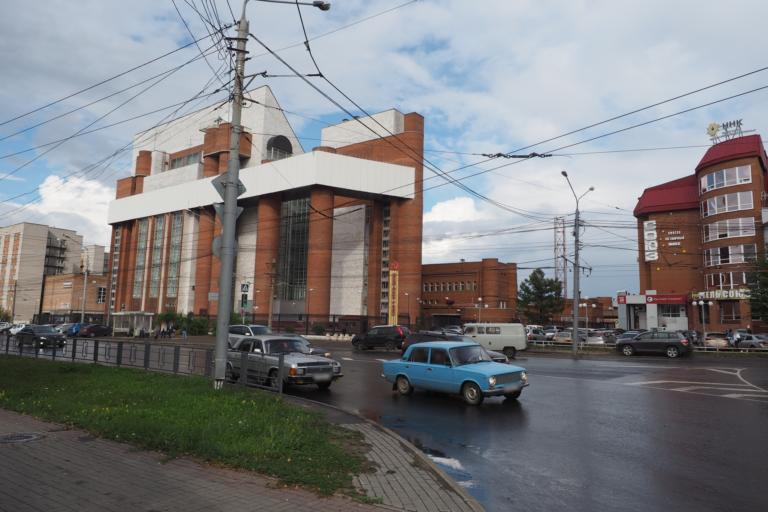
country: RU
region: Tomsk
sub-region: Tomskiy Rayon
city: Tomsk
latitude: 56.4666
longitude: 84.9812
